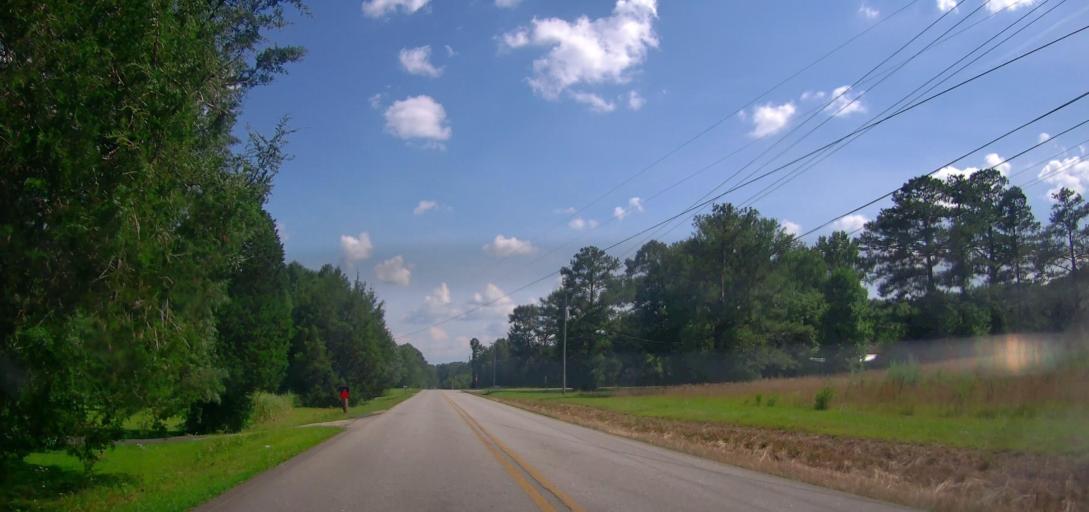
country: US
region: Georgia
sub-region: Spalding County
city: East Griffin
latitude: 33.2735
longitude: -84.1900
